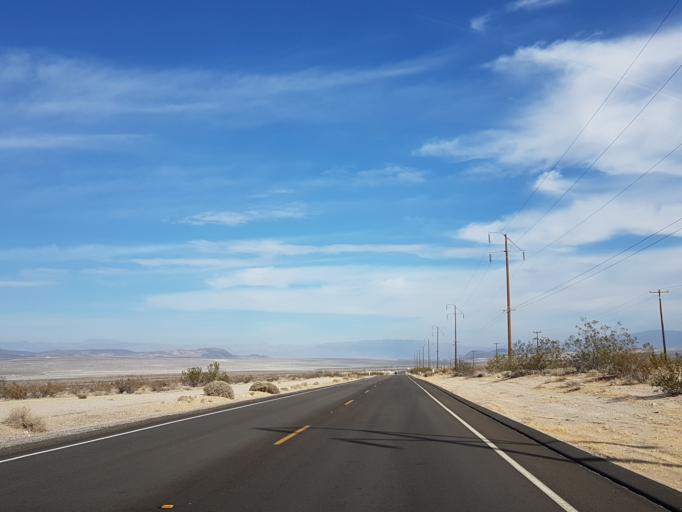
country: US
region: California
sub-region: Kern County
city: Ridgecrest
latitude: 35.6412
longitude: -117.5529
